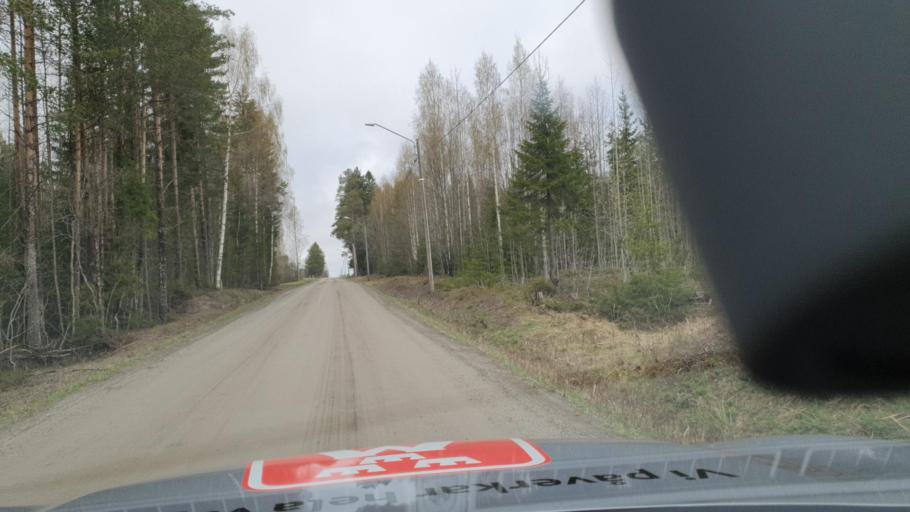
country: SE
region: Vaesterbotten
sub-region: Bjurholms Kommun
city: Bjurholm
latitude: 63.6469
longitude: 19.0530
